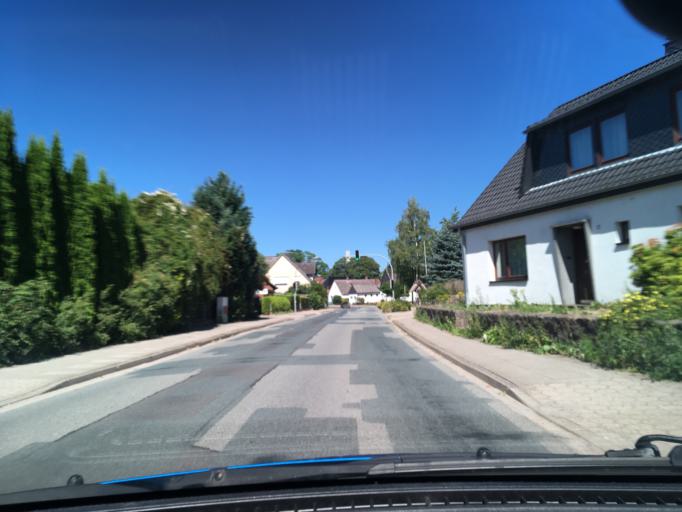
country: DE
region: Lower Saxony
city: Bendestorf
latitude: 53.3678
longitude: 9.9359
